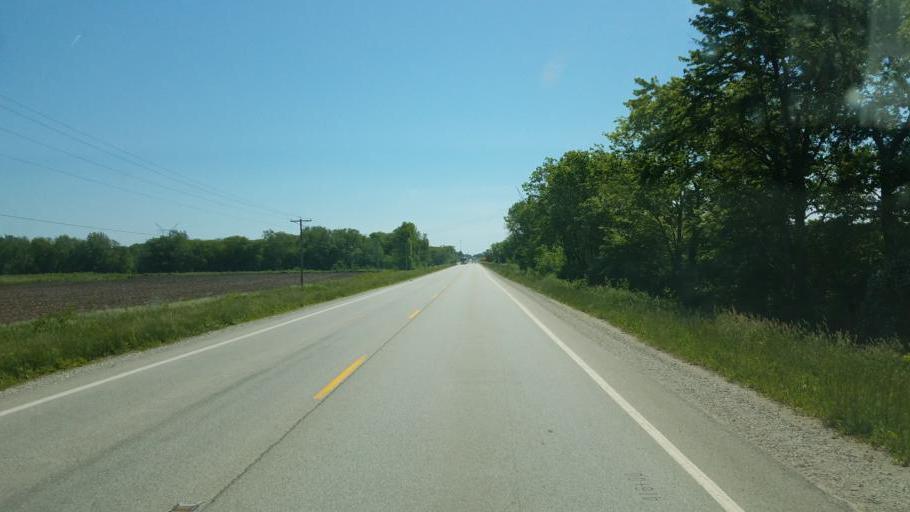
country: US
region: Illinois
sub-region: McLean County
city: Heyworth
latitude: 40.3121
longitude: -89.0190
